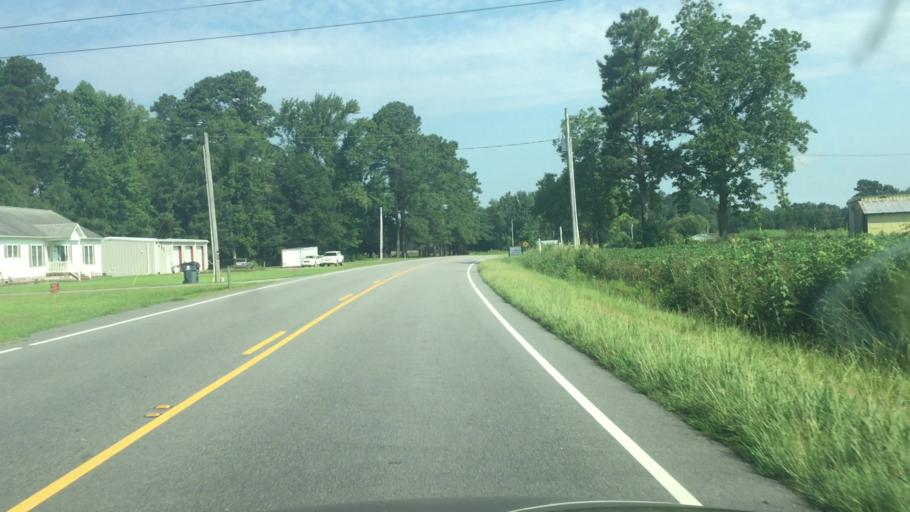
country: US
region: North Carolina
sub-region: Columbus County
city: Chadbourn
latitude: 34.2909
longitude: -78.8250
